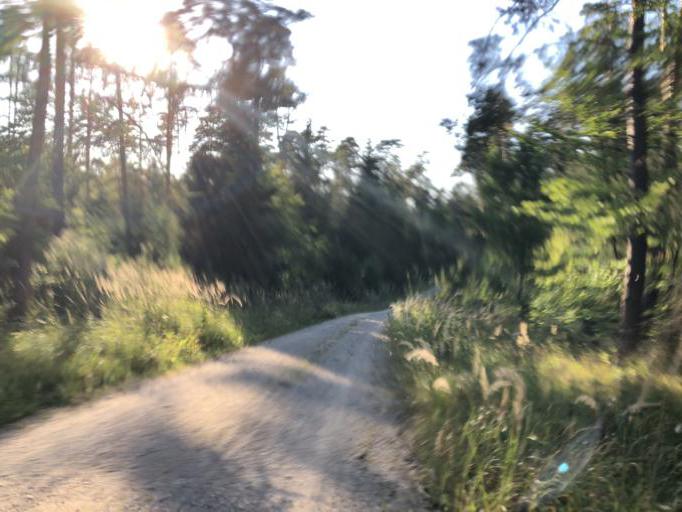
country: DE
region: Bavaria
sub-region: Regierungsbezirk Mittelfranken
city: Uttenreuth
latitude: 49.5605
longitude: 11.0897
